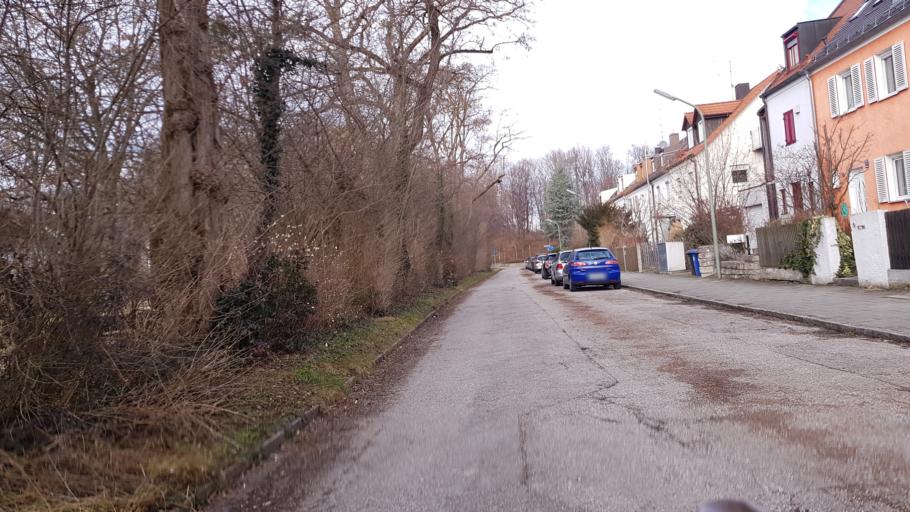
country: DE
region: Bavaria
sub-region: Upper Bavaria
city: Neuried
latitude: 48.1192
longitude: 11.5116
